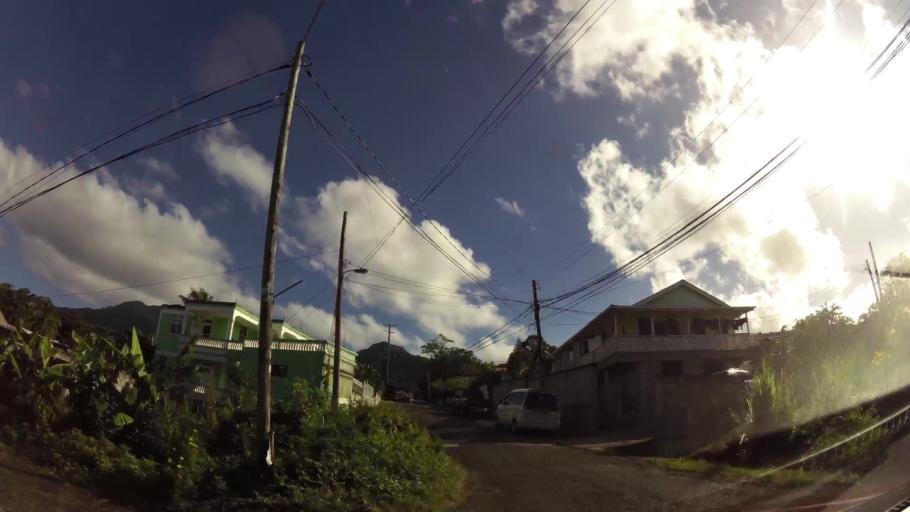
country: DM
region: Saint John
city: Portsmouth
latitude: 15.5803
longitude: -61.4578
